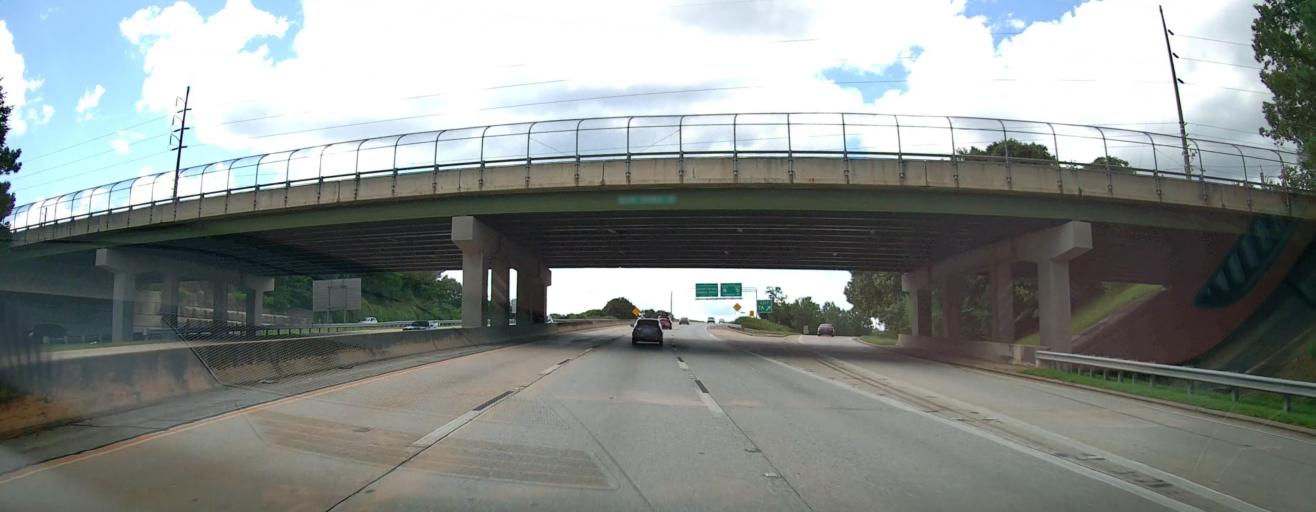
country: US
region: Georgia
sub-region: Muscogee County
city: Columbus
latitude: 32.5034
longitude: -84.9484
